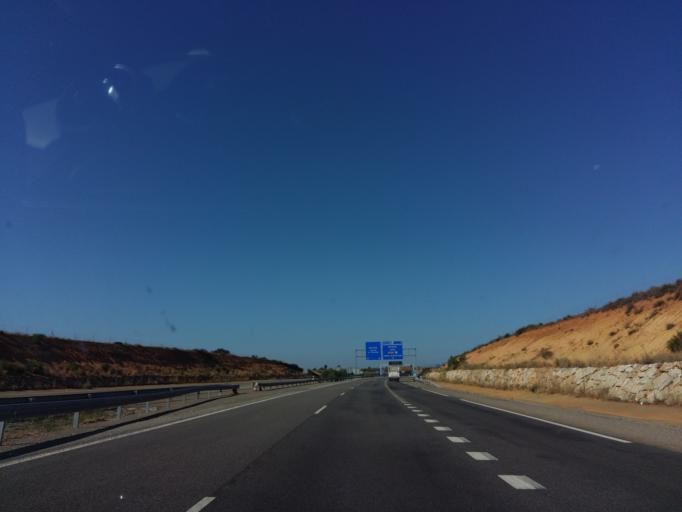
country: ES
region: Castille and Leon
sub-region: Provincia de Leon
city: San Andres del Rabanedo
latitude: 42.5733
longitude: -5.6332
